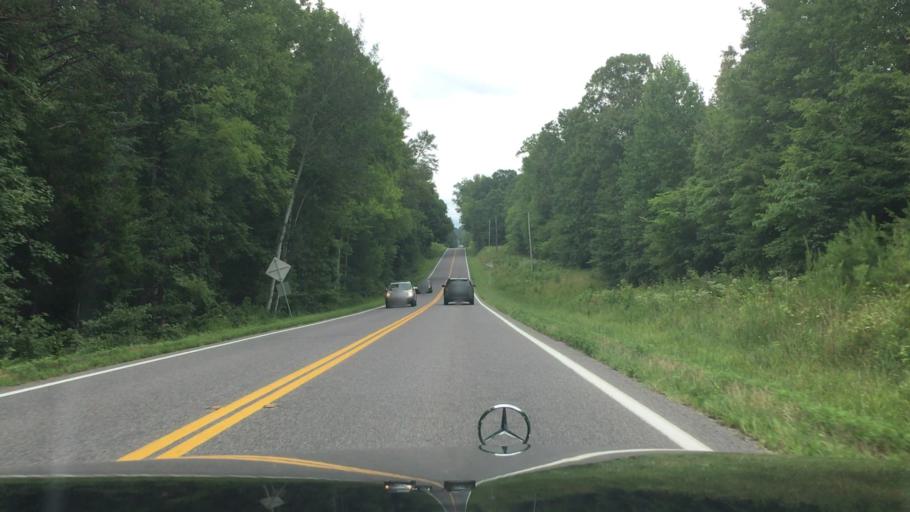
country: US
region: Virginia
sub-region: Nottoway County
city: Crewe
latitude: 37.2789
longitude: -78.1887
